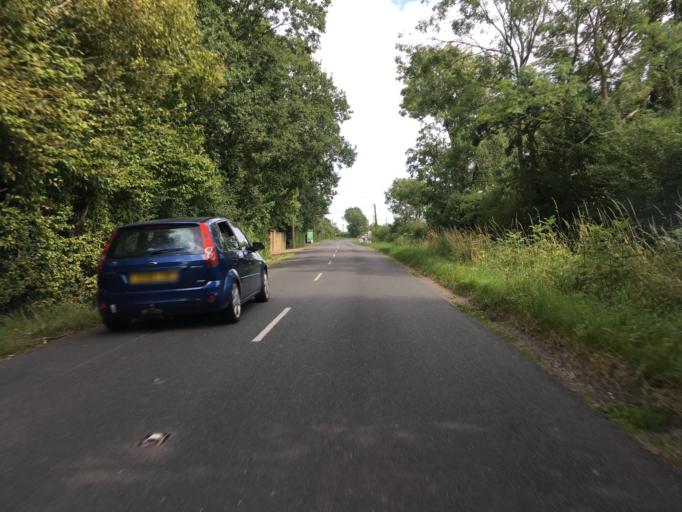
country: GB
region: England
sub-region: Kent
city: Tenterden
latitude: 51.0600
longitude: 0.7216
